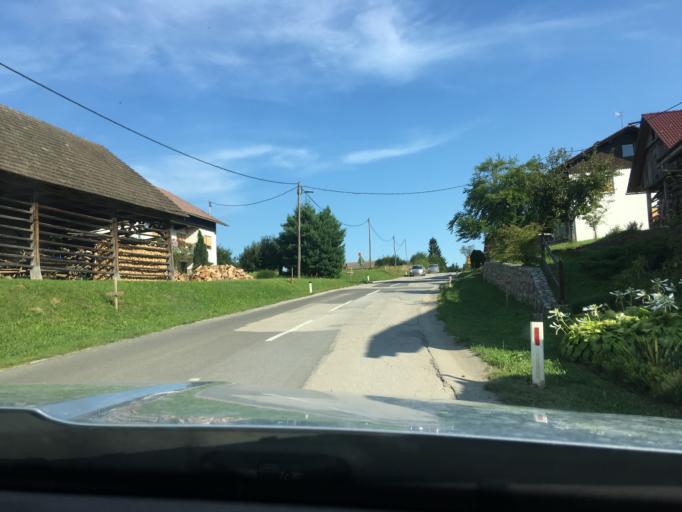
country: SI
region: Metlika
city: Metlika
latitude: 45.6144
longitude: 15.2494
